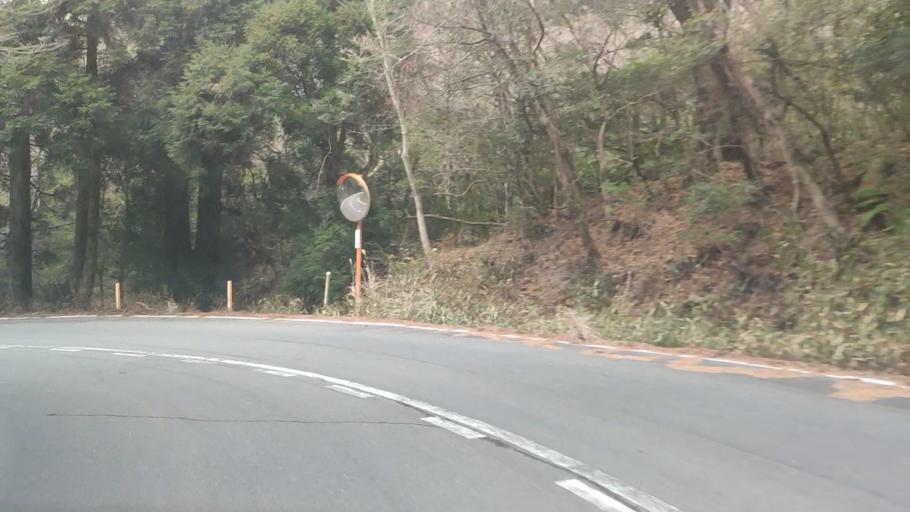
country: JP
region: Nagasaki
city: Shimabara
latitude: 32.7515
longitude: 130.2748
